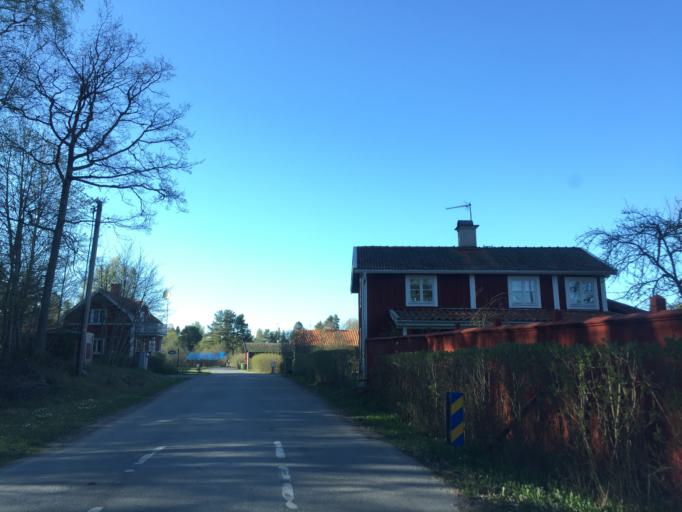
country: SE
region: OErebro
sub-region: Orebro Kommun
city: Odensbacken
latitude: 59.2256
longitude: 15.5637
